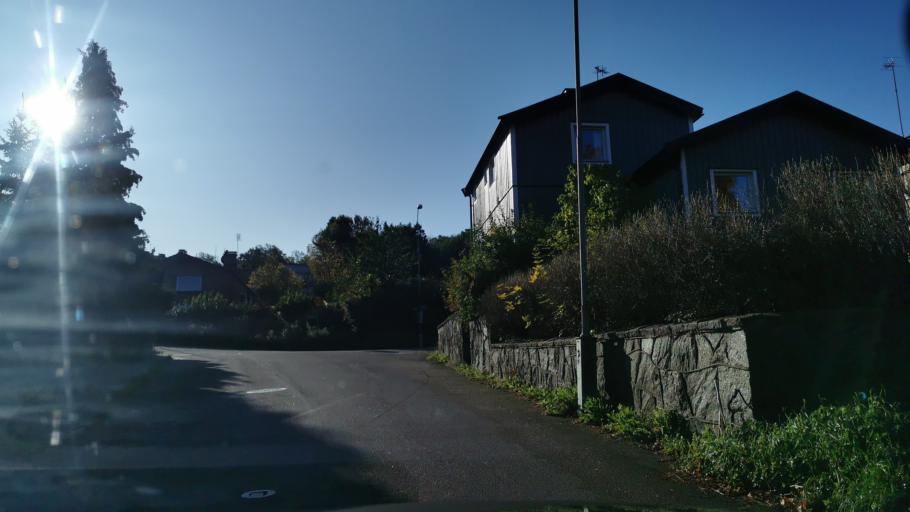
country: SE
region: Vaestra Goetaland
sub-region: Goteborg
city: Eriksbo
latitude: 57.7286
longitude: 12.0558
